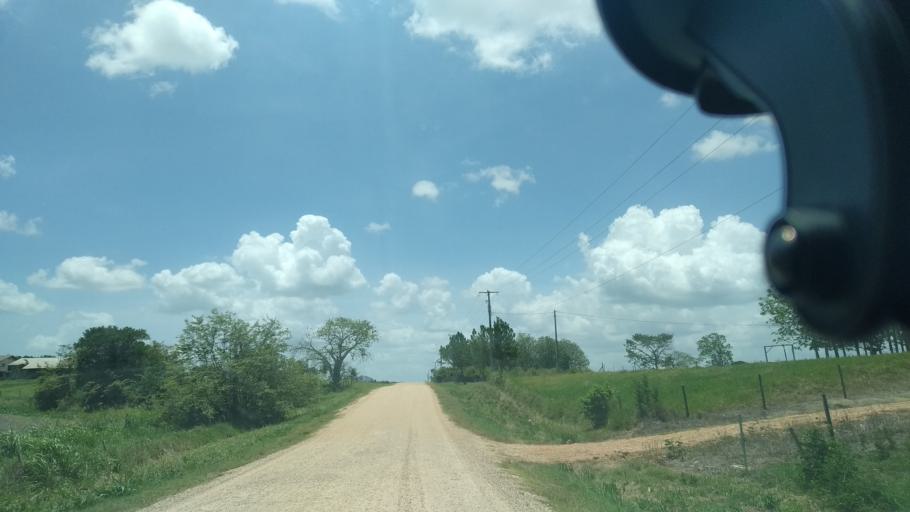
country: BZ
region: Cayo
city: San Ignacio
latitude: 17.2343
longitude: -88.9876
